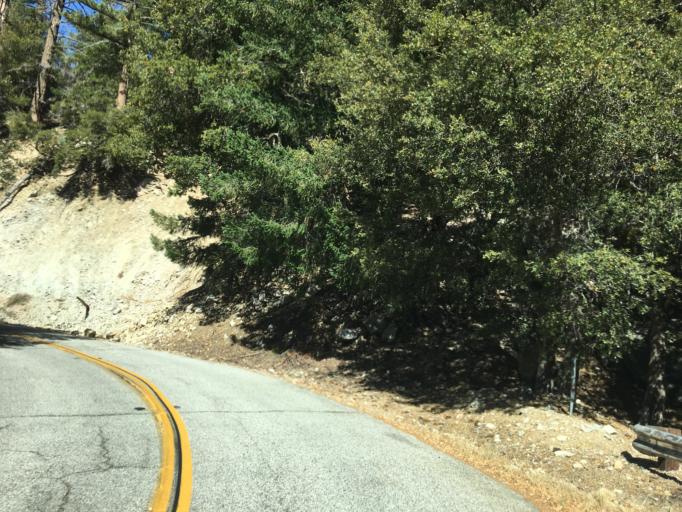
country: US
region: California
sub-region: Los Angeles County
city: Glendora
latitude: 34.3179
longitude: -117.8365
